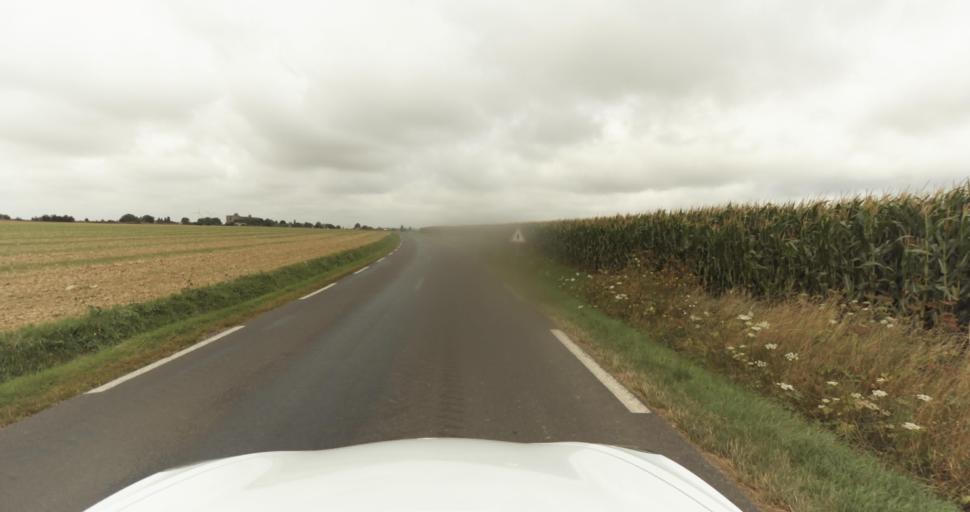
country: FR
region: Haute-Normandie
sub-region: Departement de l'Eure
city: Claville
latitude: 49.0849
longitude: 1.0507
